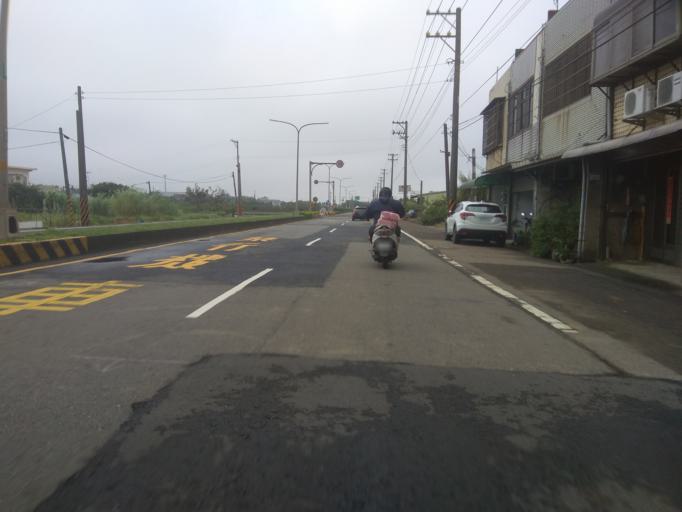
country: TW
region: Taiwan
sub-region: Hsinchu
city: Zhubei
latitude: 25.0124
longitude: 121.0492
